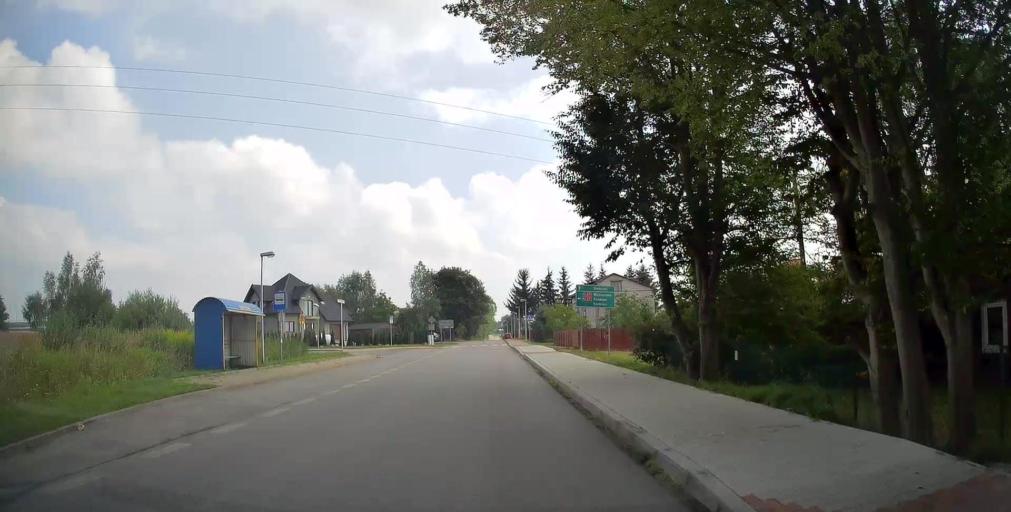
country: PL
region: Masovian Voivodeship
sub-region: Powiat bialobrzeski
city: Sucha
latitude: 51.6091
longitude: 20.9775
